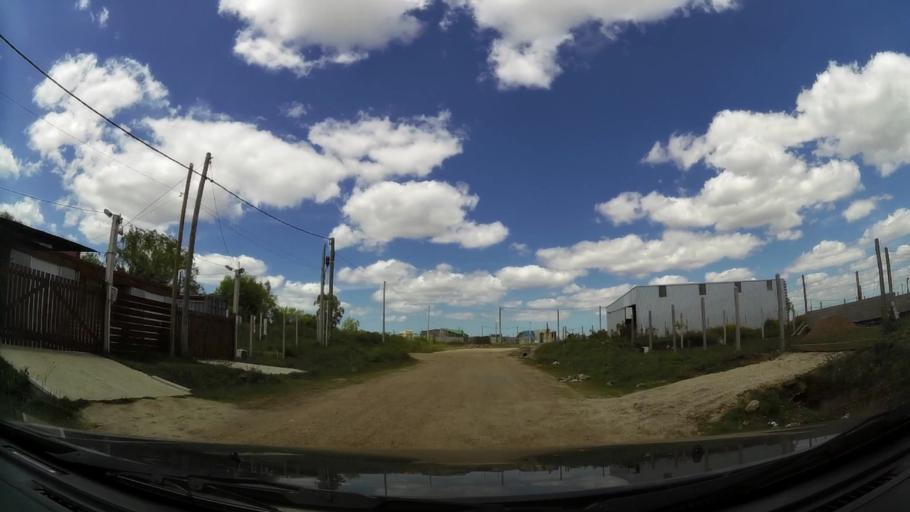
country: UY
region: Canelones
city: Colonia Nicolich
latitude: -34.8203
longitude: -56.0152
